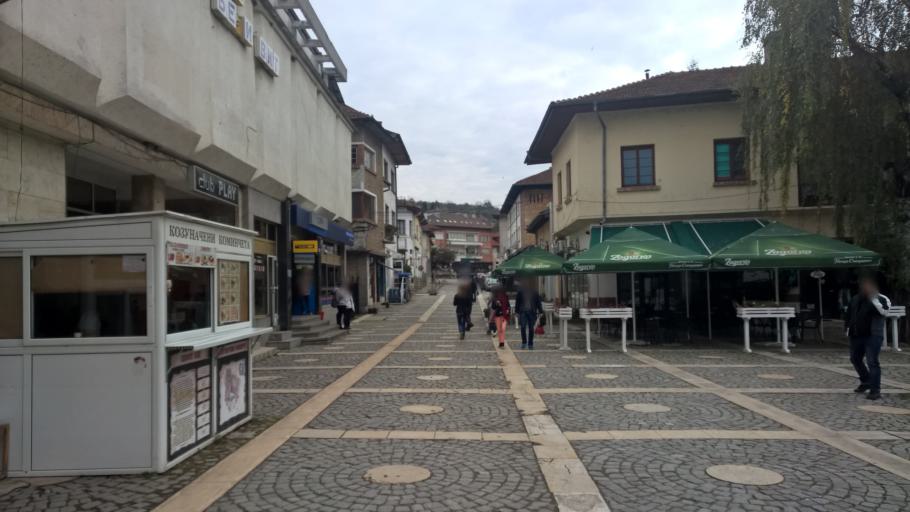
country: BG
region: Lovech
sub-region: Obshtina Teteven
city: Teteven
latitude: 42.9183
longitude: 24.2651
